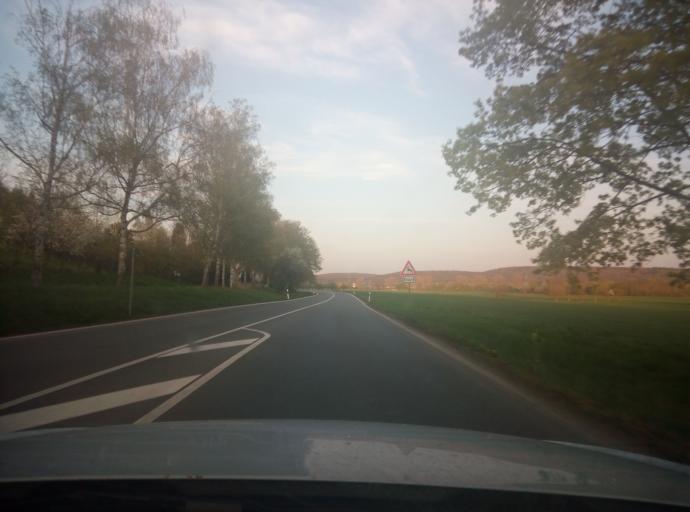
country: DE
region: Baden-Wuerttemberg
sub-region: Tuebingen Region
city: Tuebingen
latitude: 48.5019
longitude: 9.0063
